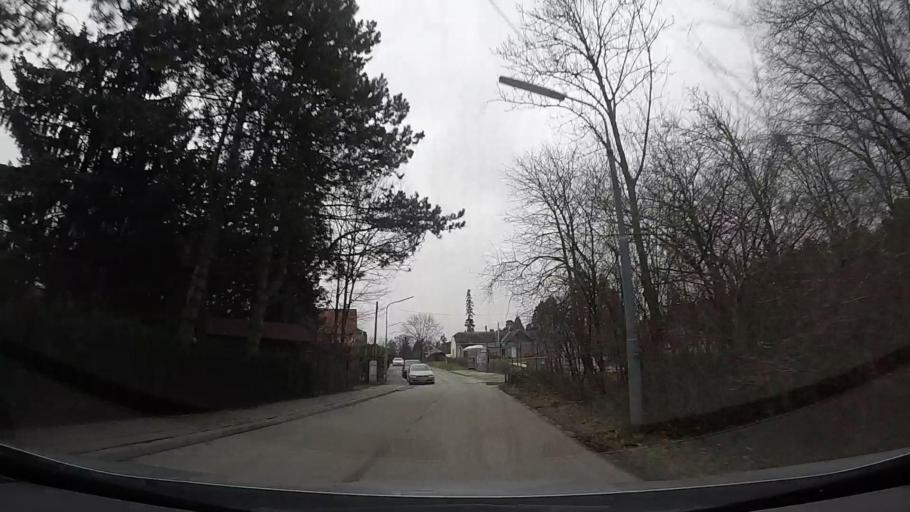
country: AT
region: Lower Austria
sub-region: Politischer Bezirk Wien-Umgebung
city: Purkersdorf
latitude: 48.2197
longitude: 16.2406
